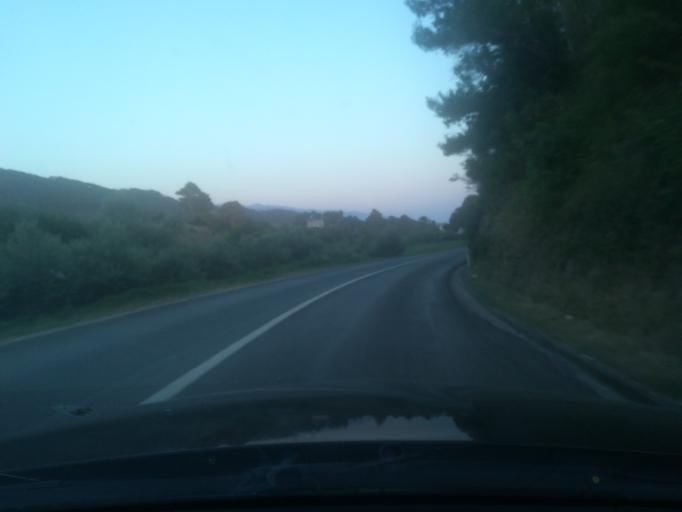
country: HR
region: Primorsko-Goranska
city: Banjol
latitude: 44.7578
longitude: 14.7728
